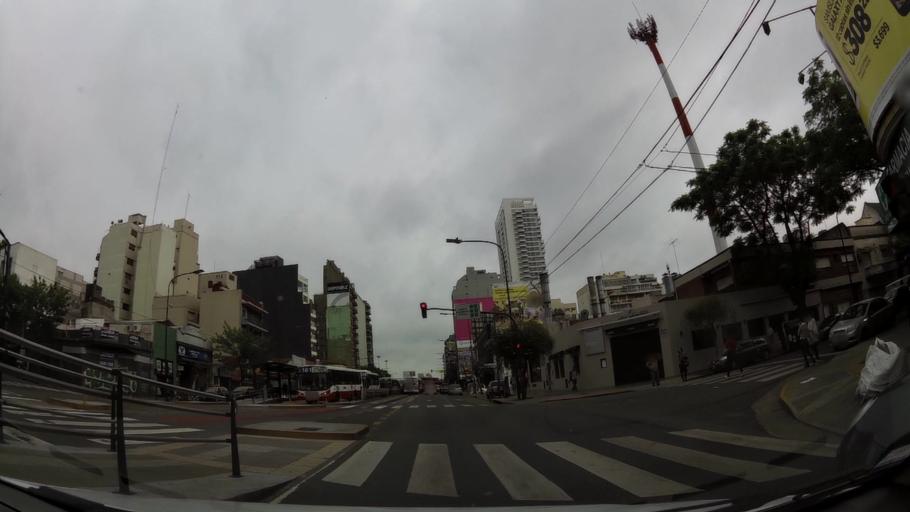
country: AR
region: Buenos Aires
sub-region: Partido de Vicente Lopez
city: Olivos
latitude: -34.5423
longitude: -58.4731
